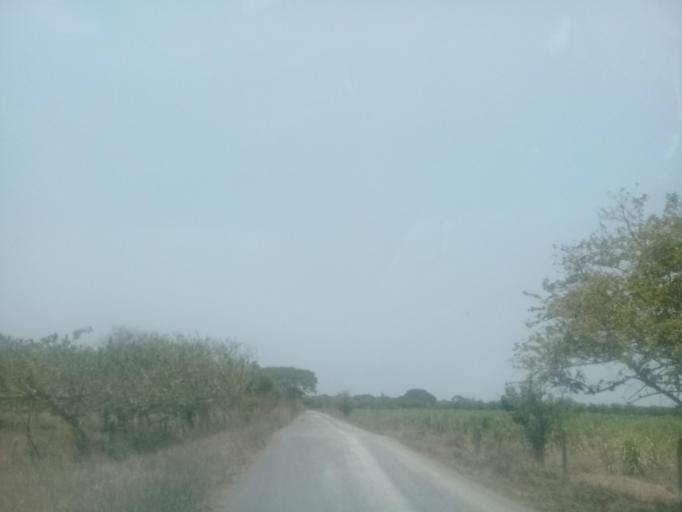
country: MX
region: Veracruz
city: Jamapa
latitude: 19.0809
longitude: -96.2390
